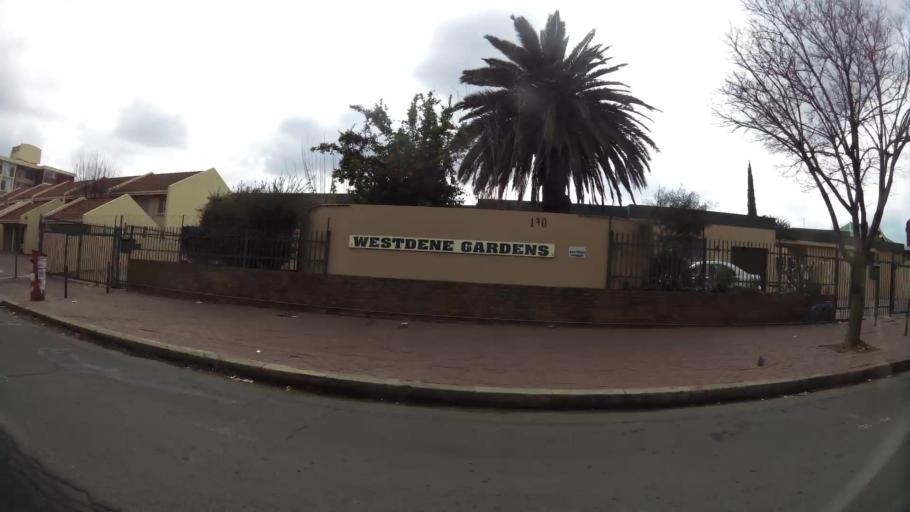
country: ZA
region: Orange Free State
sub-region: Mangaung Metropolitan Municipality
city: Bloemfontein
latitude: -29.1112
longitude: 26.2109
